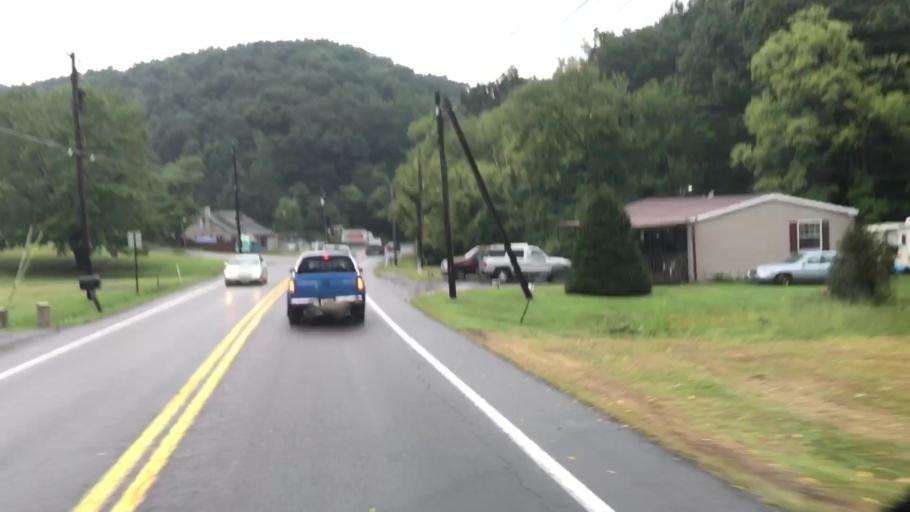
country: US
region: Pennsylvania
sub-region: Cumberland County
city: Schlusser
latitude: 40.3020
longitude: -77.1495
